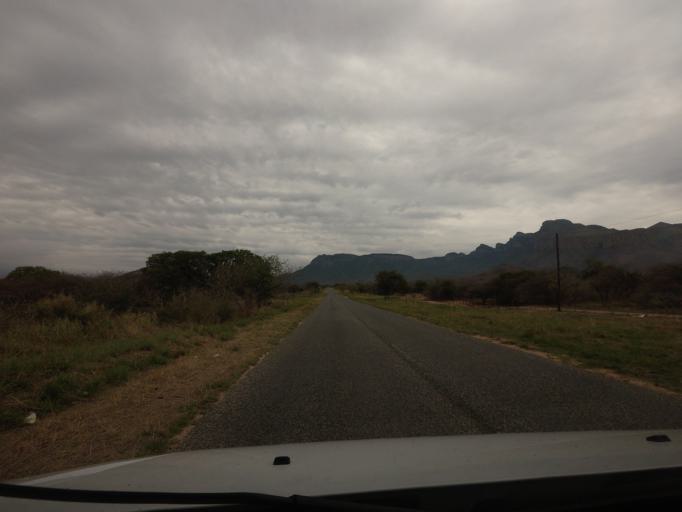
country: ZA
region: Limpopo
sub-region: Mopani District Municipality
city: Hoedspruit
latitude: -24.4899
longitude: 30.8902
